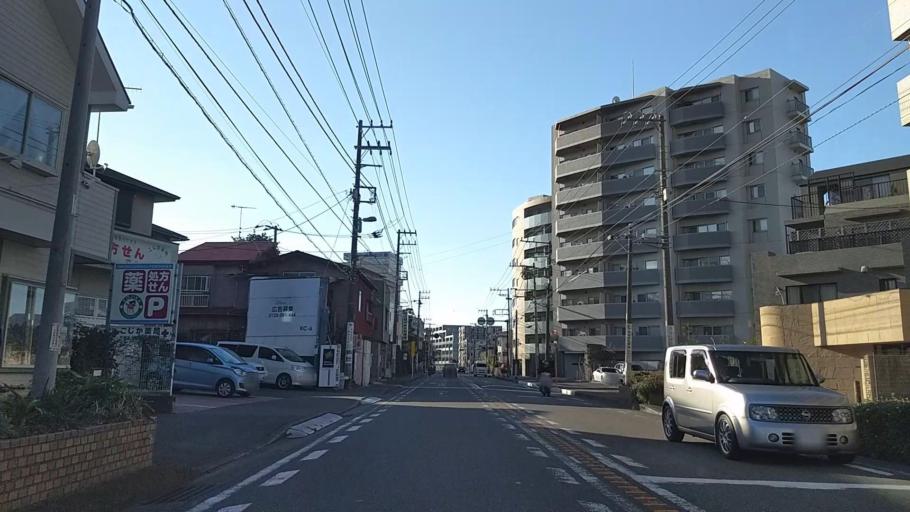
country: JP
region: Kanagawa
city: Fujisawa
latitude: 35.3212
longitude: 139.4861
